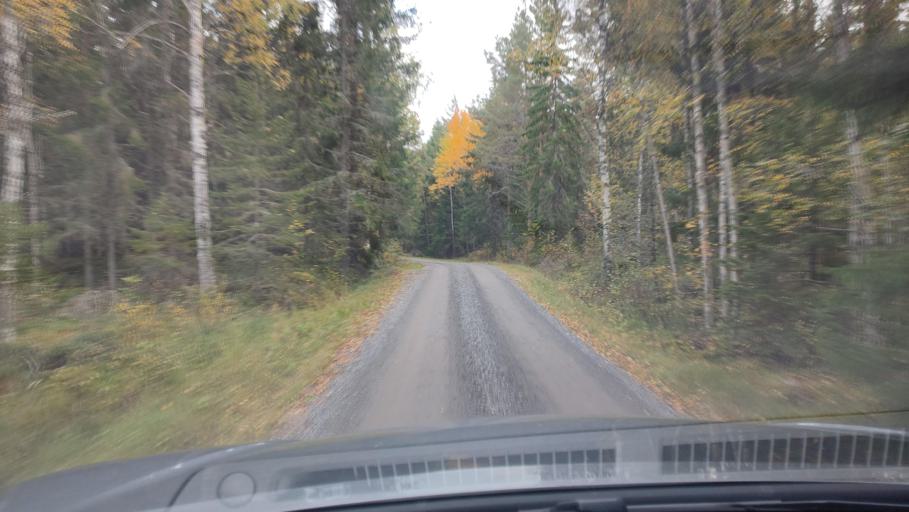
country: FI
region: Ostrobothnia
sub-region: Sydosterbotten
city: Kristinestad
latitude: 62.2358
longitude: 21.3994
